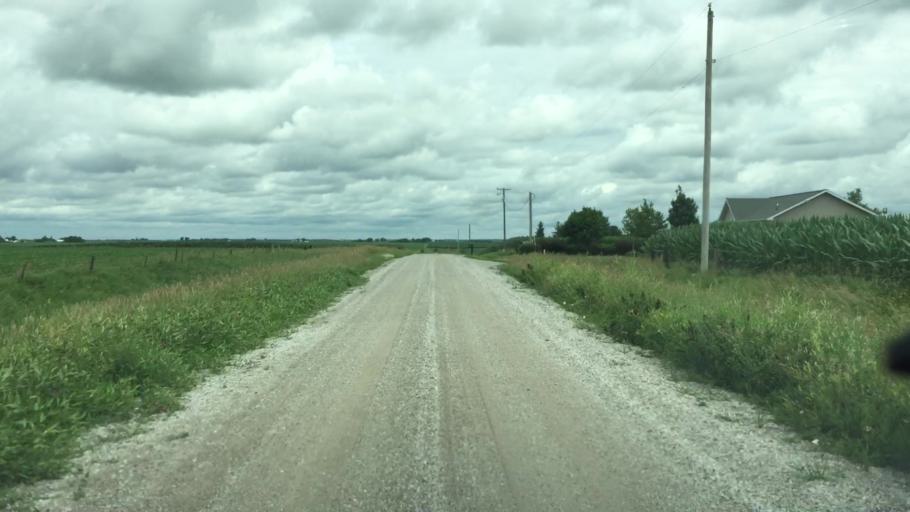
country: US
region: Iowa
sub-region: Jasper County
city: Monroe
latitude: 41.5749
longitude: -93.1208
